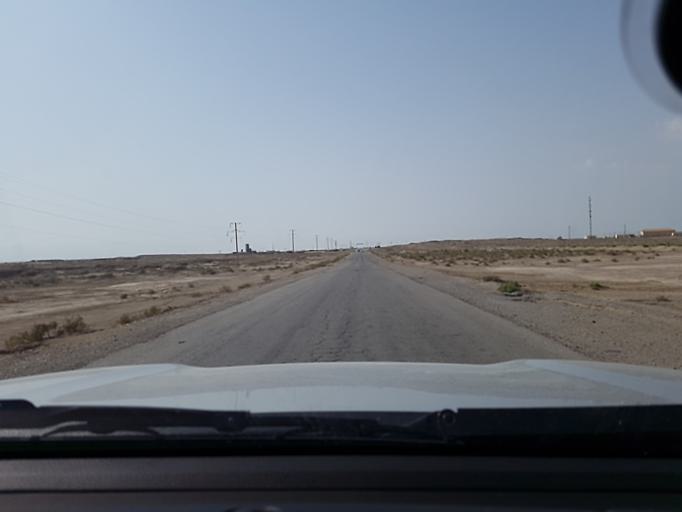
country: TM
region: Balkan
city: Gumdag
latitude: 39.1228
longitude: 54.5795
